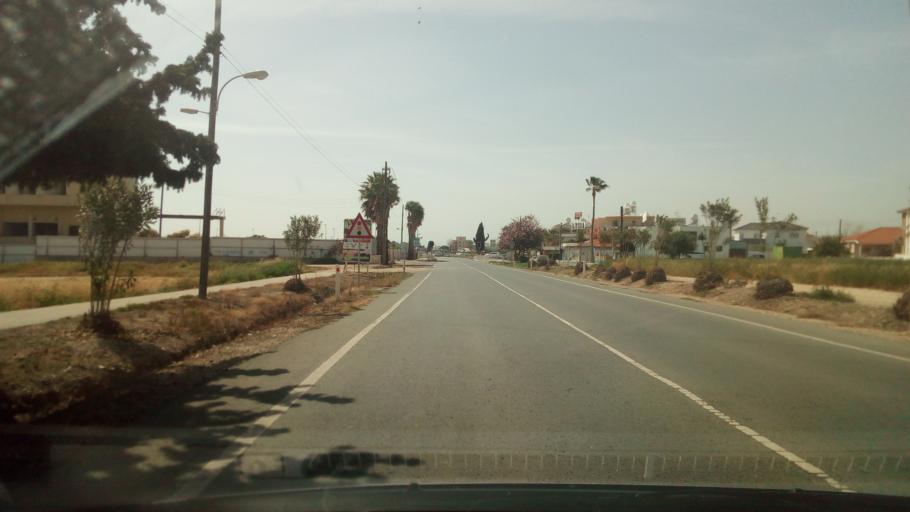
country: CY
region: Larnaka
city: Voroklini
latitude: 34.9776
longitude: 33.6870
